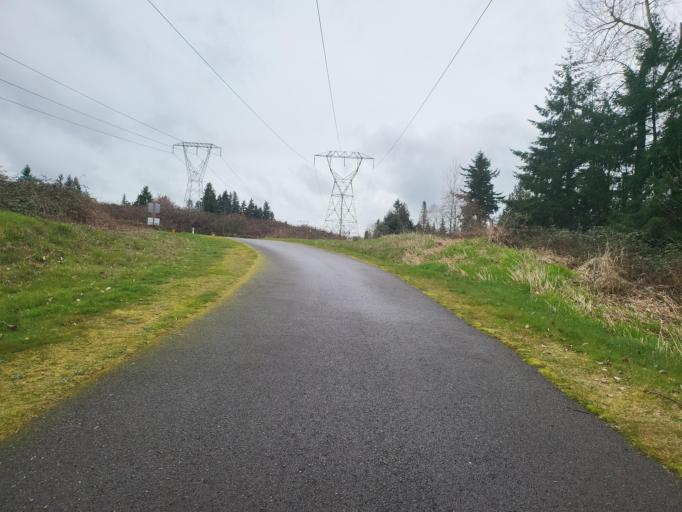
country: US
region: Washington
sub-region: King County
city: East Hill-Meridian
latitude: 47.4227
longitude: -122.1717
